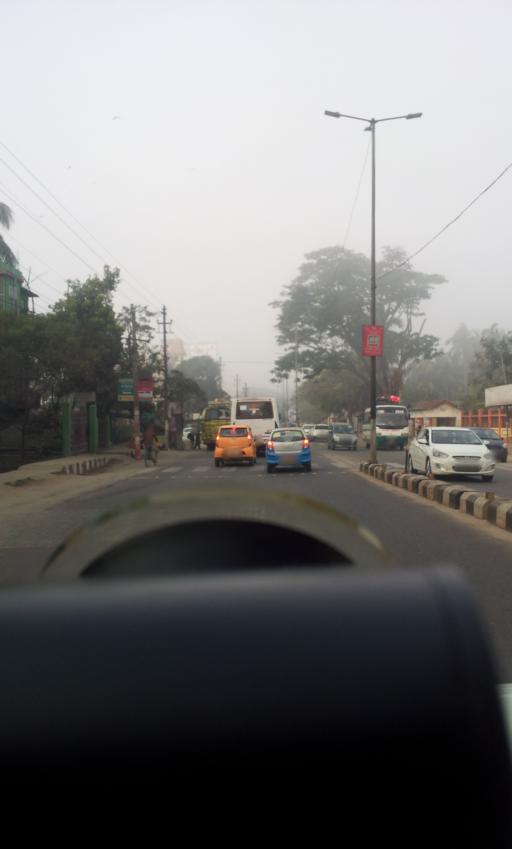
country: IN
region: Assam
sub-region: Kamrup Metropolitan
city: Guwahati
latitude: 26.1721
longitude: 91.7278
